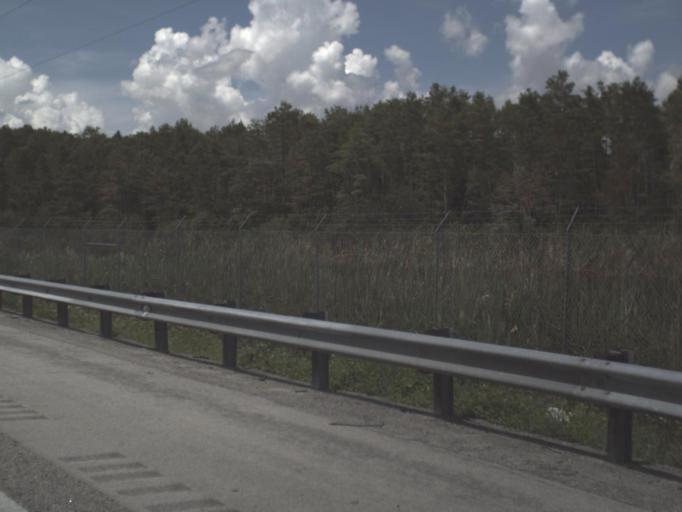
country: US
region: Florida
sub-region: Collier County
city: Immokalee
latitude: 26.1678
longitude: -81.1509
